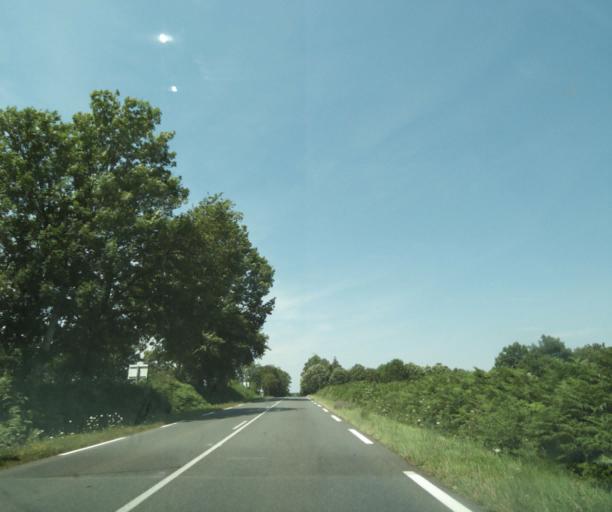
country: FR
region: Limousin
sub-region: Departement de la Haute-Vienne
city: Peyrat-de-Bellac
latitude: 46.1332
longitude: 0.9873
